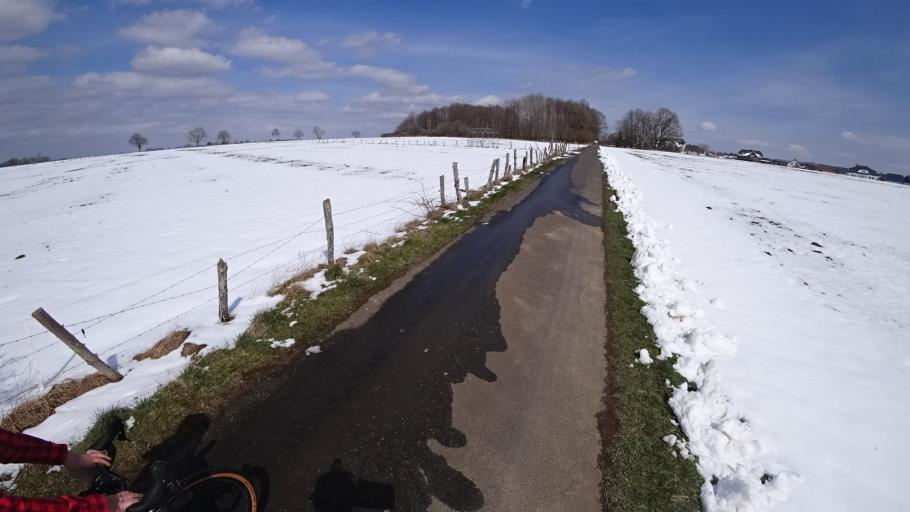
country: DE
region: Rheinland-Pfalz
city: Elkenroth
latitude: 50.7223
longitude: 7.8769
